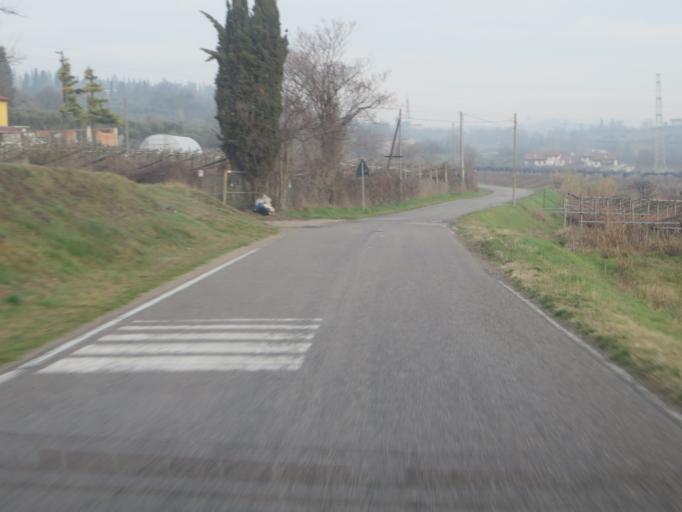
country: IT
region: Veneto
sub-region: Provincia di Verona
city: Sandra
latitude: 45.4594
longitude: 10.8190
